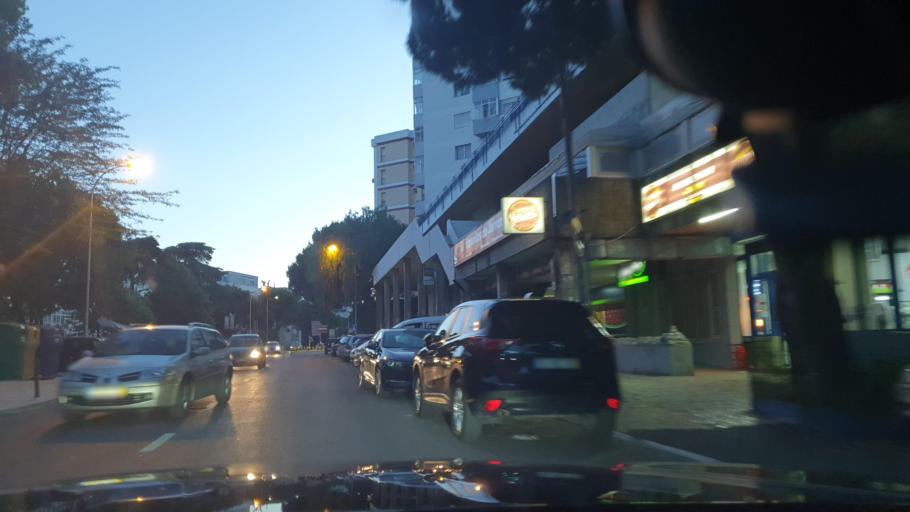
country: PT
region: Lisbon
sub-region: Sintra
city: Queluz
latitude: 38.7612
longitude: -9.2598
